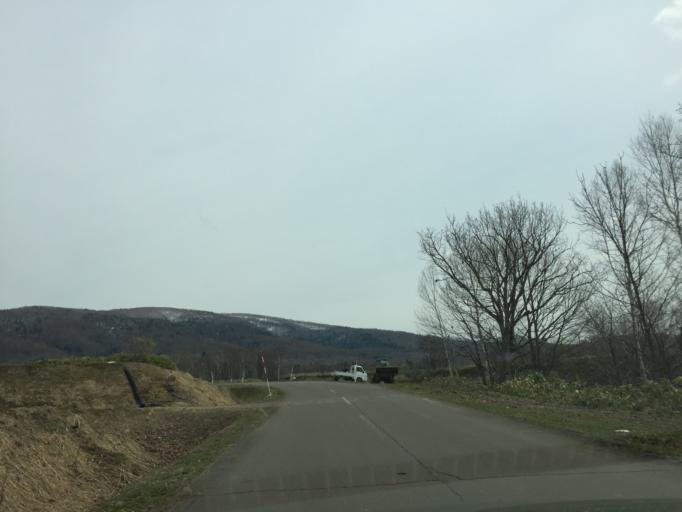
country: JP
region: Hokkaido
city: Ashibetsu
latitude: 43.6090
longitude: 142.2127
